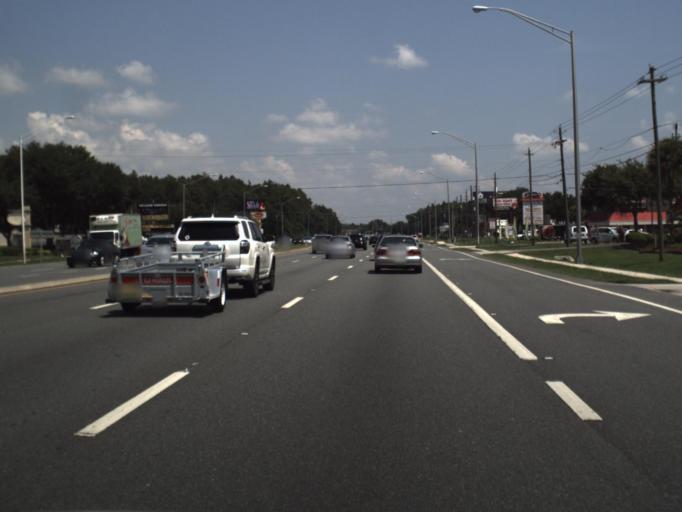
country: US
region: Florida
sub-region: Hillsborough County
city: Carrollwood
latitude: 28.0539
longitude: -82.5039
